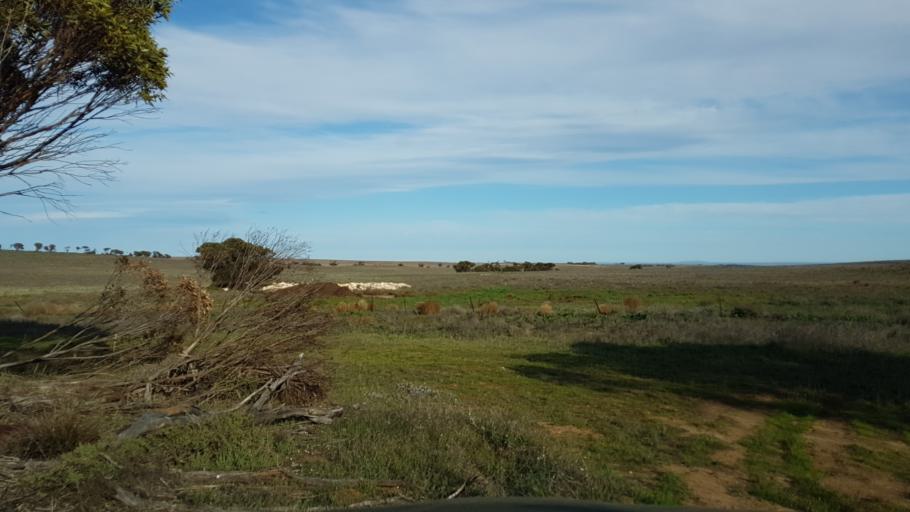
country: AU
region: South Australia
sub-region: Murray Bridge
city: Tailem Bend
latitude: -35.0651
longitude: 139.4654
